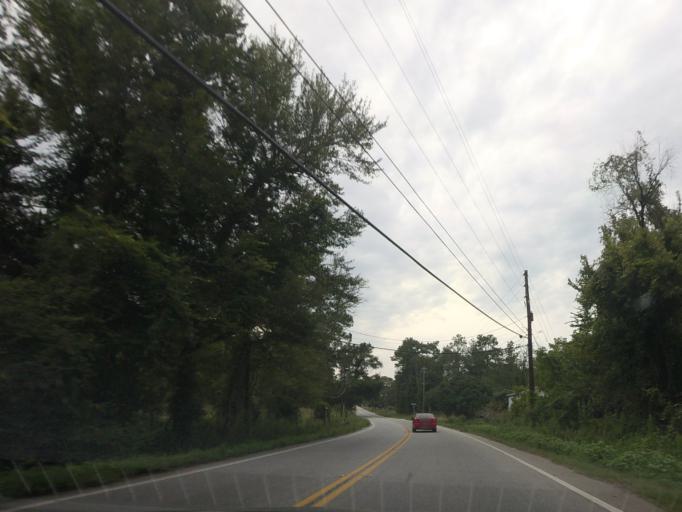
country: US
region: Georgia
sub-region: Bibb County
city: Macon
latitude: 32.8043
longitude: -83.5028
